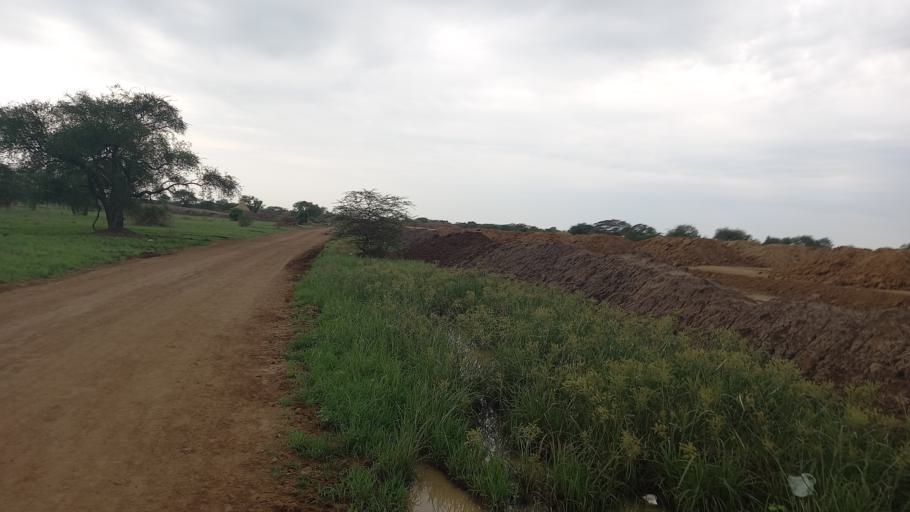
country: ET
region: Gambela
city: Gambela
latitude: 8.3338
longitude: 33.9477
